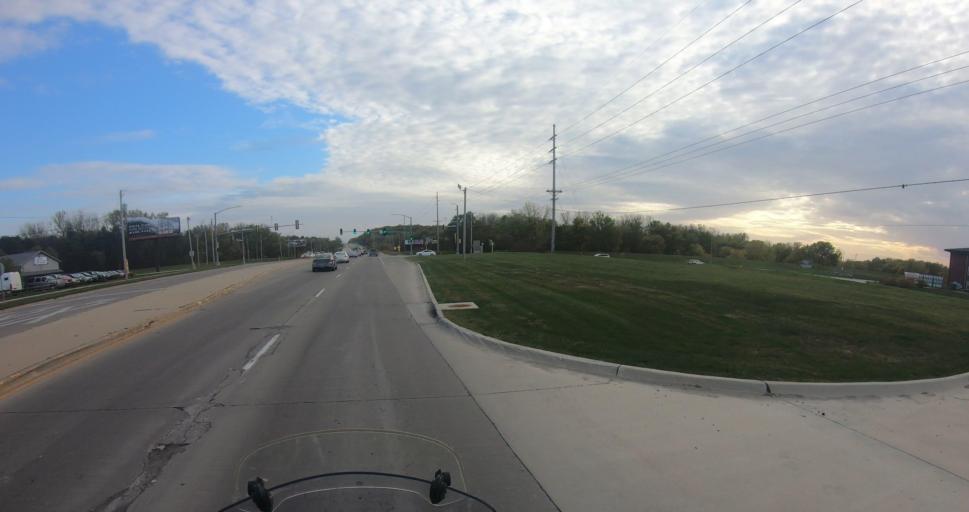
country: US
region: Iowa
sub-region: Polk County
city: West Des Moines
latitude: 41.5683
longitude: -93.7031
